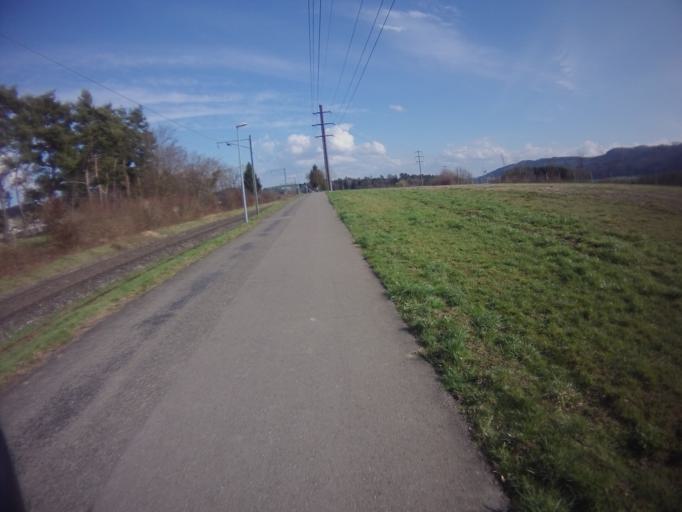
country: CH
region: Aargau
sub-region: Bezirk Baden
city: Neuenhof
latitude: 47.4539
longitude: 8.3355
